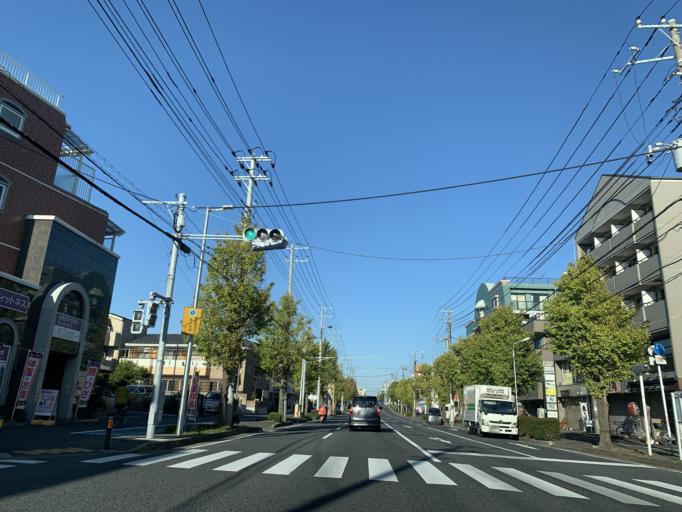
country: JP
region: Tokyo
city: Urayasu
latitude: 35.6574
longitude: 139.8954
